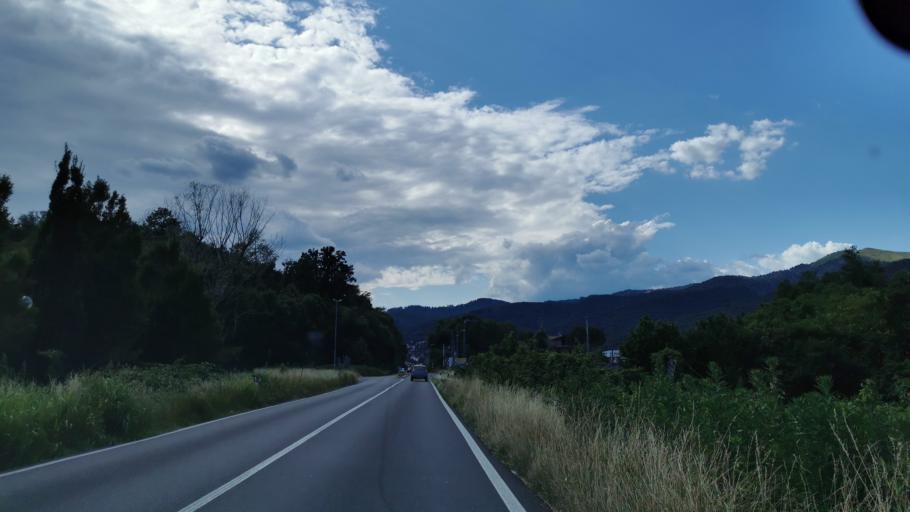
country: IT
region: Lombardy
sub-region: Provincia di Como
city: Albese Con Cassano
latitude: 45.7905
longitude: 9.1556
